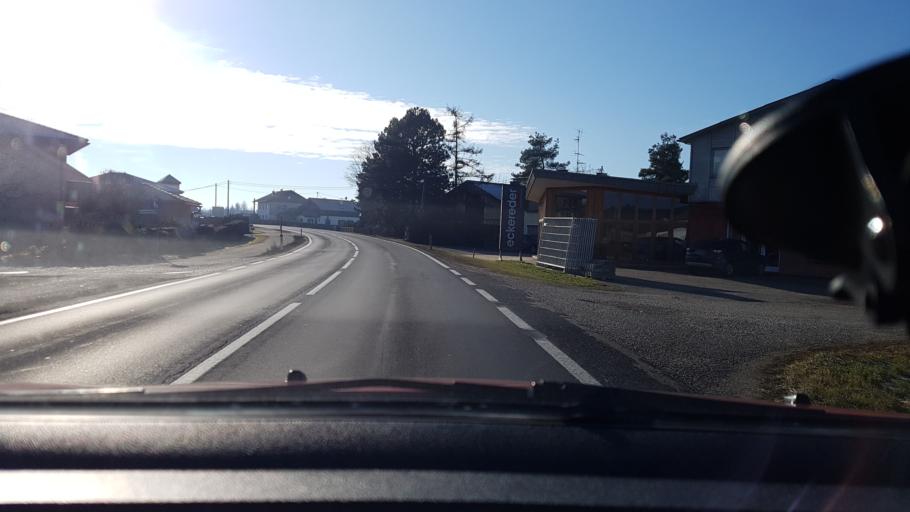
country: AT
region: Upper Austria
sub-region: Politischer Bezirk Braunau am Inn
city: Braunau am Inn
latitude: 48.1842
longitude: 13.0559
